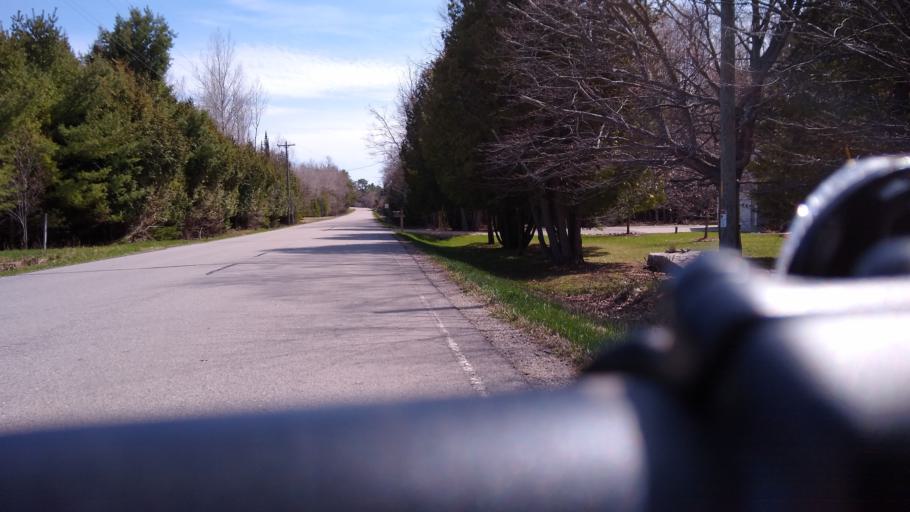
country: US
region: Michigan
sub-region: Delta County
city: Escanaba
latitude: 45.6919
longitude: -87.1526
